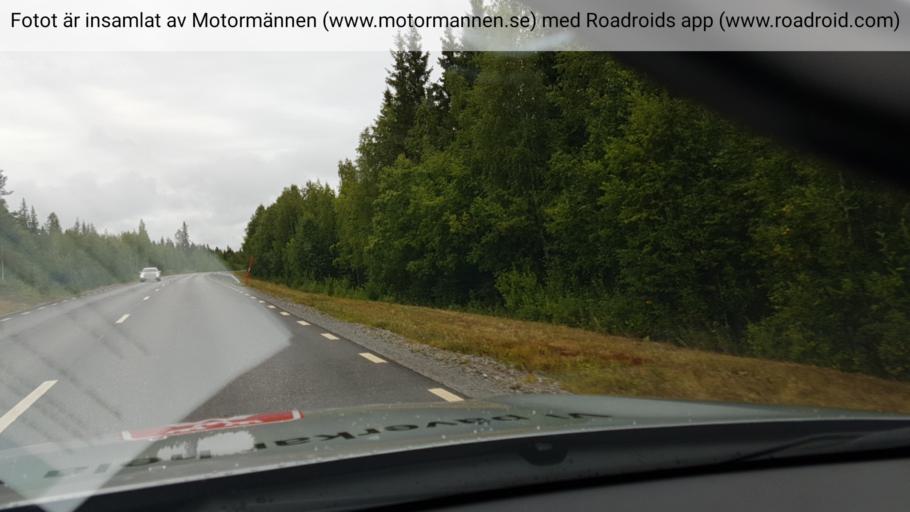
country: SE
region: Norrbotten
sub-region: Alvsbyns Kommun
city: AElvsbyn
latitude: 66.3192
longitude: 20.7839
